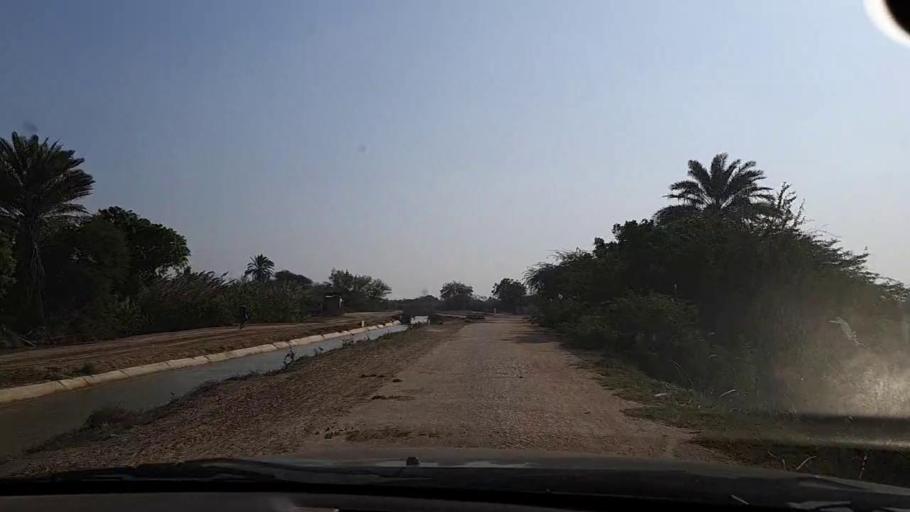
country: PK
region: Sindh
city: Mirpur Sakro
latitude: 24.3136
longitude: 67.7027
